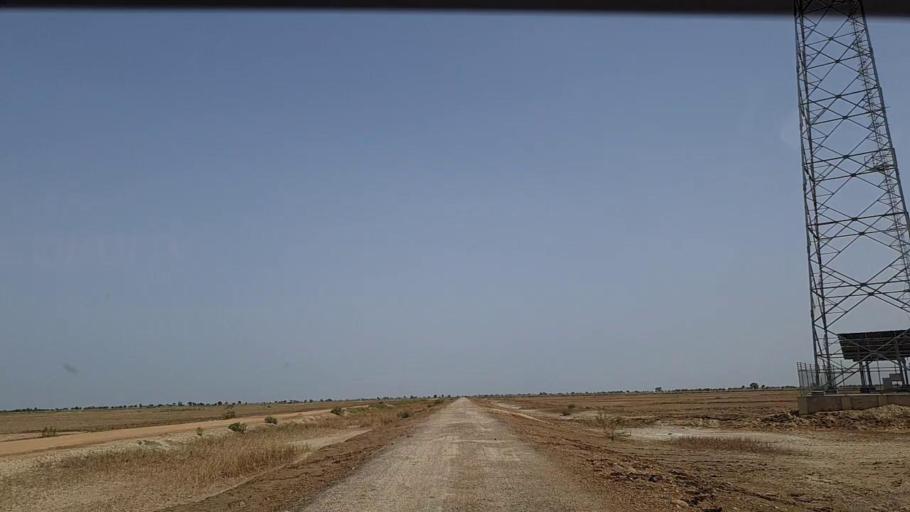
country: PK
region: Sindh
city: Phulji
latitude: 26.7889
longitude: 67.6439
